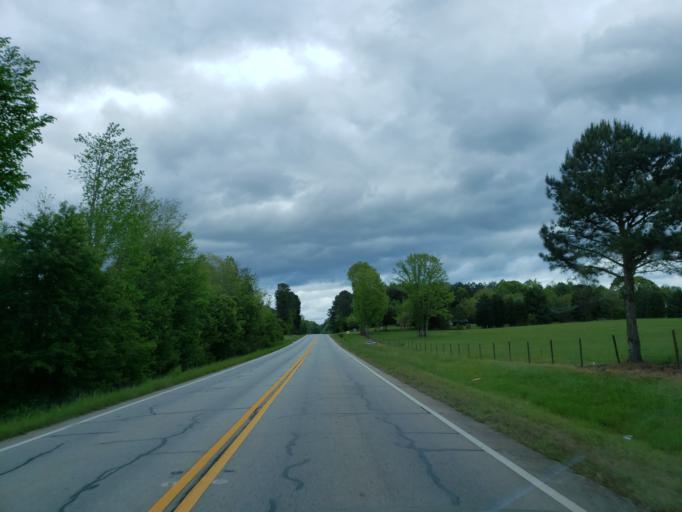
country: US
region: Georgia
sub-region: Carroll County
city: Temple
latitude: 33.8274
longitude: -85.0534
